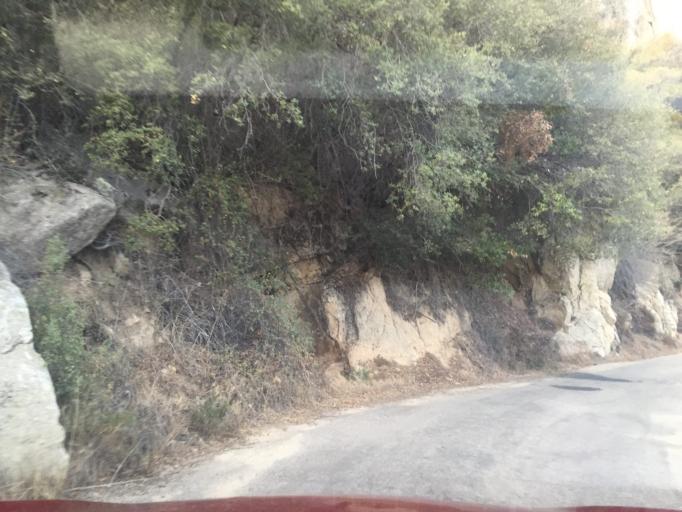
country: US
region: California
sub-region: Tulare County
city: Three Rivers
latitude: 36.4312
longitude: -118.7569
